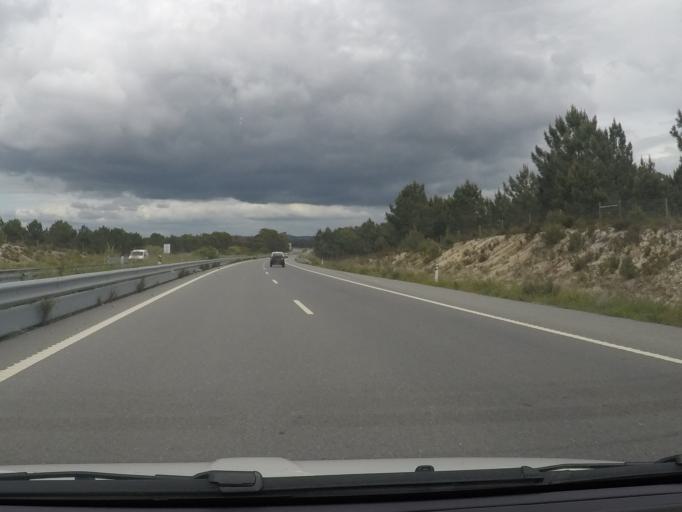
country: PT
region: Setubal
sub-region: Sines
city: Sines
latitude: 37.9785
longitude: -8.7991
